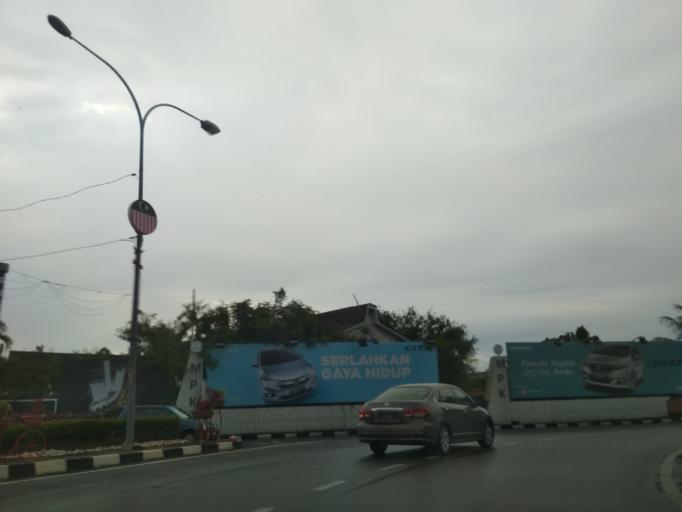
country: MY
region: Perlis
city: Kangar
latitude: 6.4447
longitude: 100.2046
